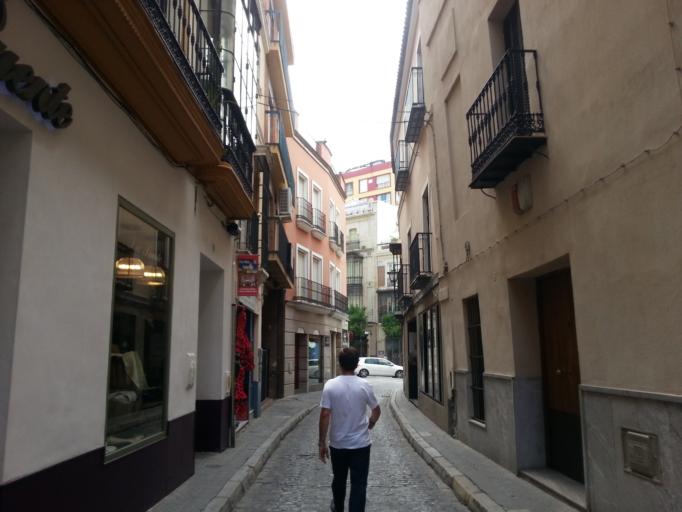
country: ES
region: Andalusia
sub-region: Provincia de Sevilla
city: Sevilla
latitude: 37.3908
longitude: -5.9983
